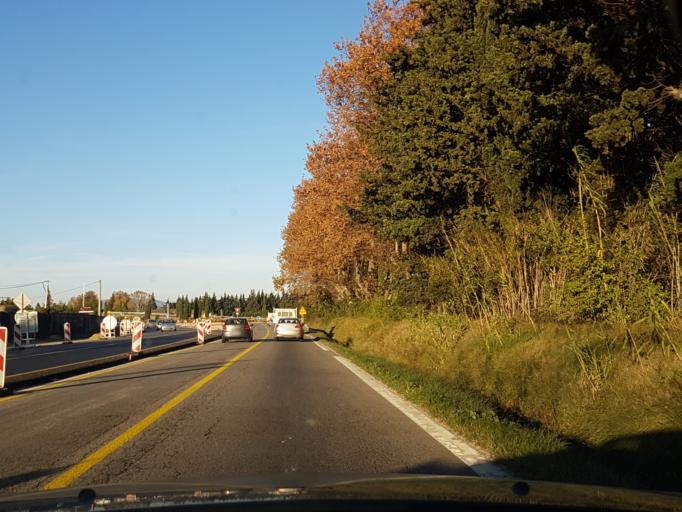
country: FR
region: Provence-Alpes-Cote d'Azur
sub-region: Departement du Vaucluse
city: Althen-des-Paluds
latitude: 44.0252
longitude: 4.9668
